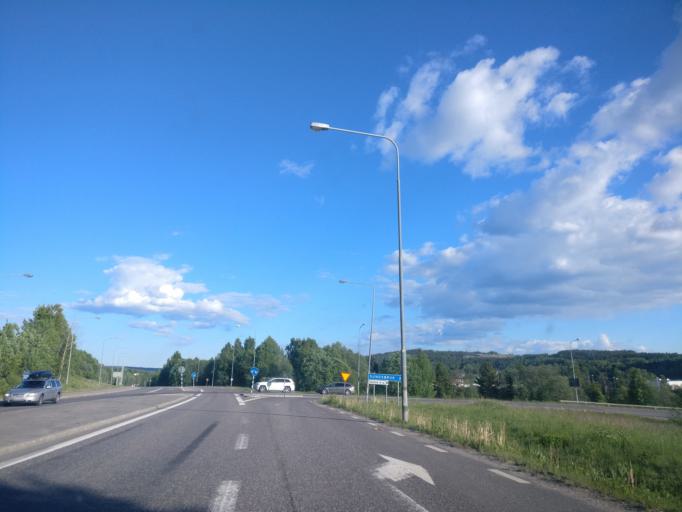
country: SE
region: Vaesternorrland
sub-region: Sundsvalls Kommun
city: Sundsbruk
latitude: 62.4465
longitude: 17.3450
